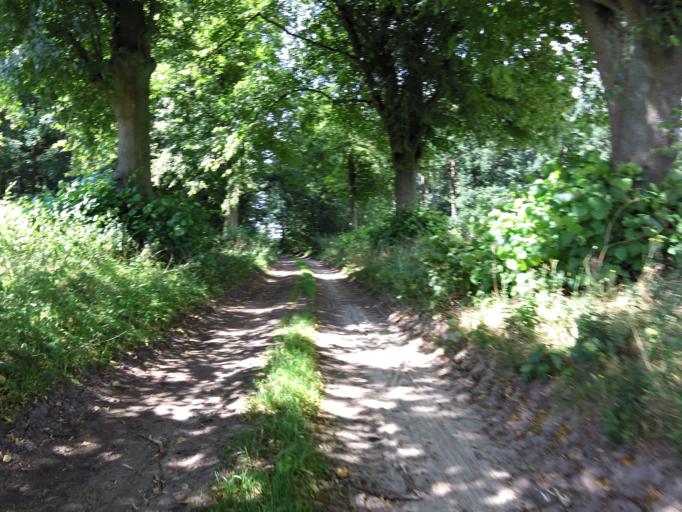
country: DE
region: Brandenburg
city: Templin
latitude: 53.1261
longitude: 13.3985
